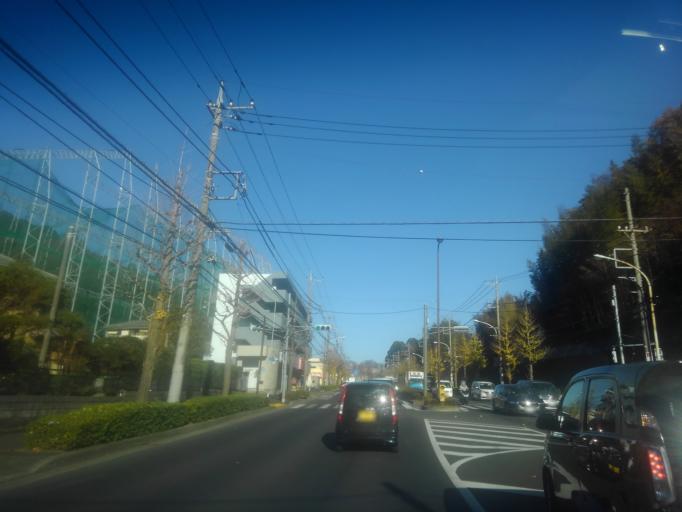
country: JP
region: Tokyo
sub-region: Machida-shi
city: Machida
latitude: 35.6049
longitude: 139.4447
